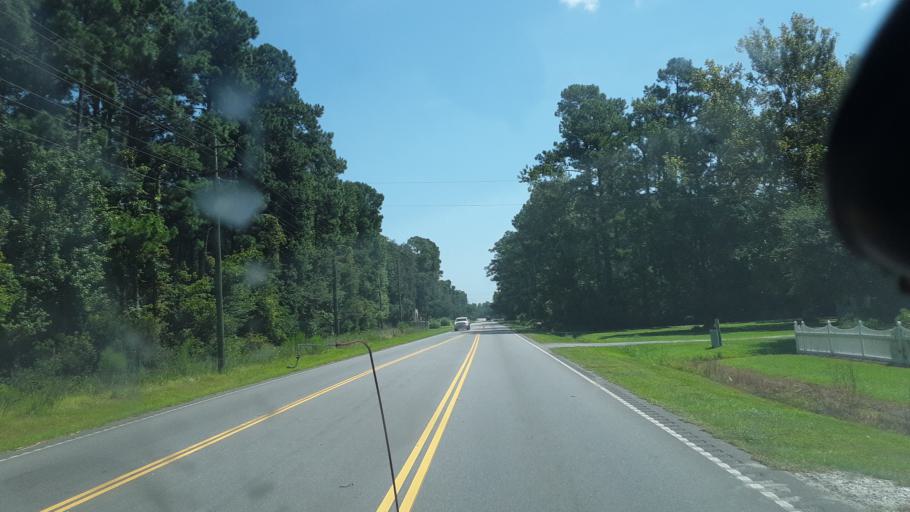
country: US
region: South Carolina
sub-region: Horry County
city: Red Hill
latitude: 33.8220
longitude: -78.9128
